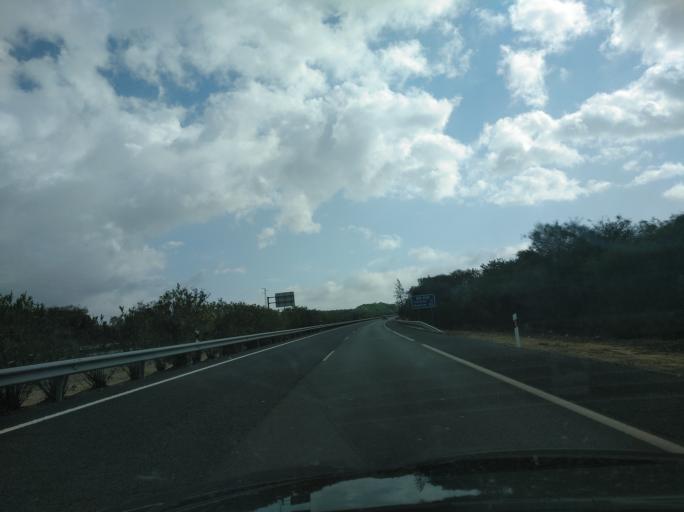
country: ES
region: Andalusia
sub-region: Provincia de Huelva
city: Cartaya
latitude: 37.3300
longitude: -7.1436
